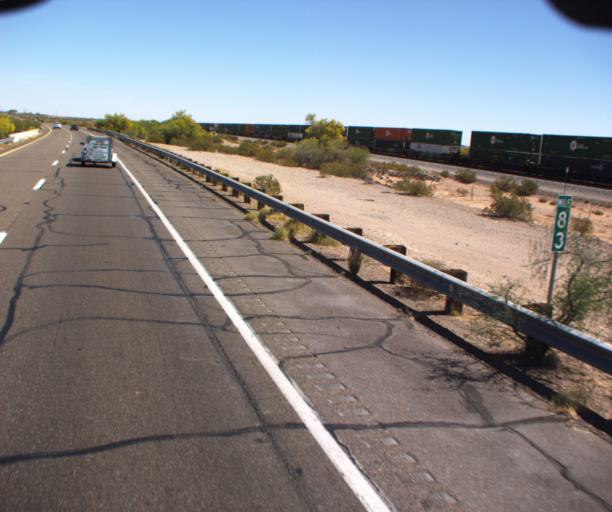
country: US
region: Arizona
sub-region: Maricopa County
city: Gila Bend
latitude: 32.8453
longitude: -113.2805
